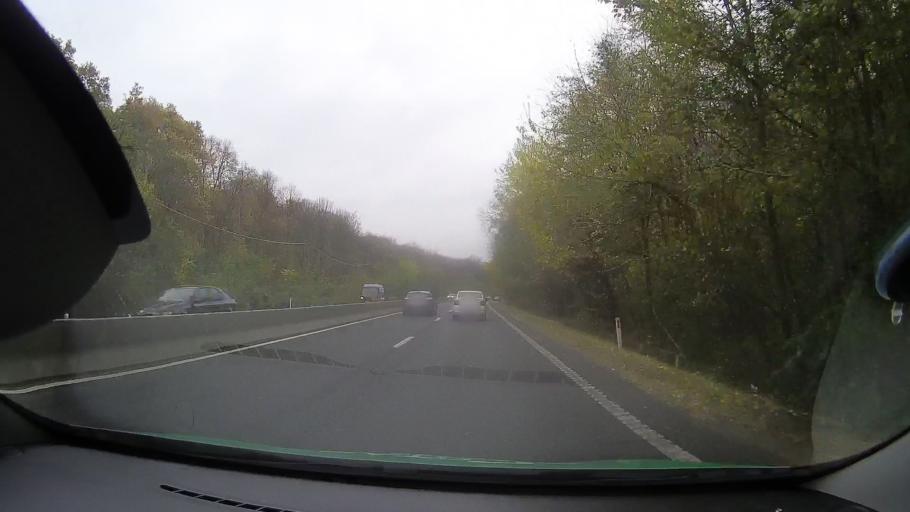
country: RO
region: Ilfov
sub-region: Comuna Ciolpani
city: Ciolpani
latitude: 44.7043
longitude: 26.0914
